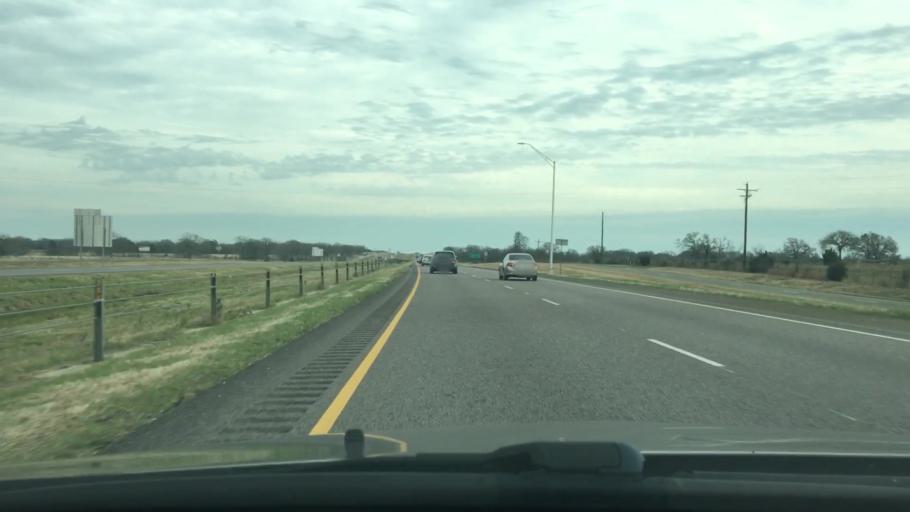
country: US
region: Texas
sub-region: Madison County
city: Madisonville
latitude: 30.9579
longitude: -95.8746
